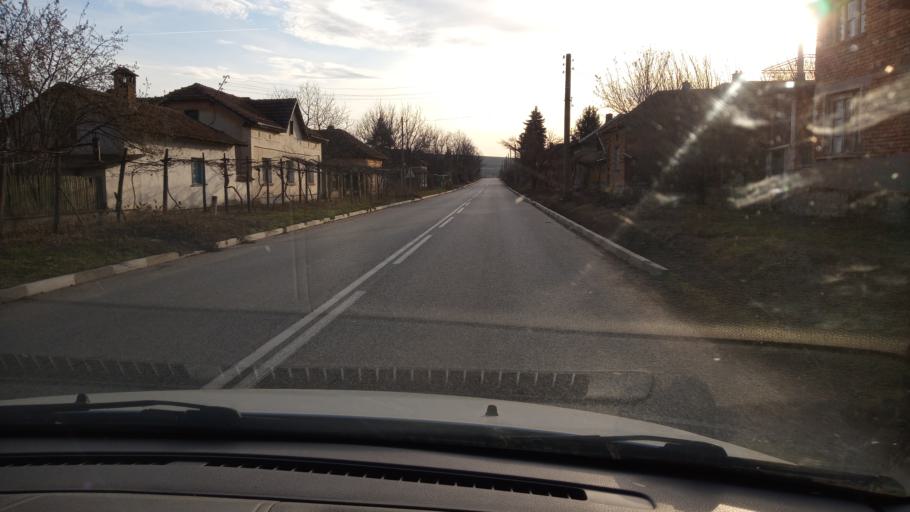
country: BG
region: Pleven
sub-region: Obshtina Pleven
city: Slavyanovo
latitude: 43.5529
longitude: 24.8647
